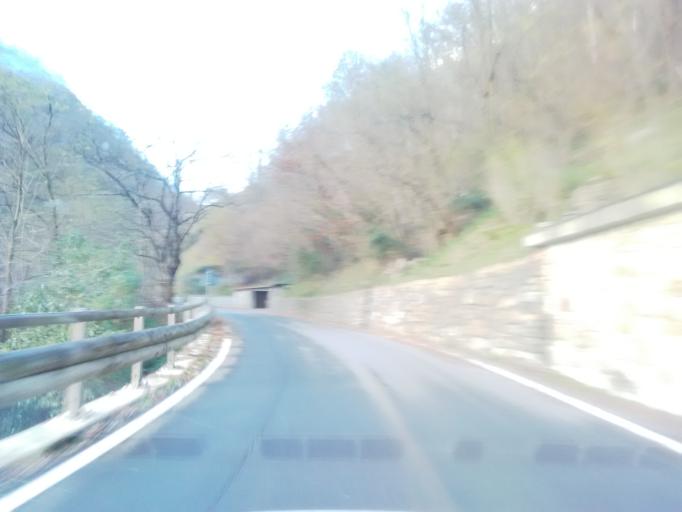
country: IT
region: Piedmont
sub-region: Provincia di Vercelli
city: Cravagliana
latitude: 45.8629
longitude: 8.1918
